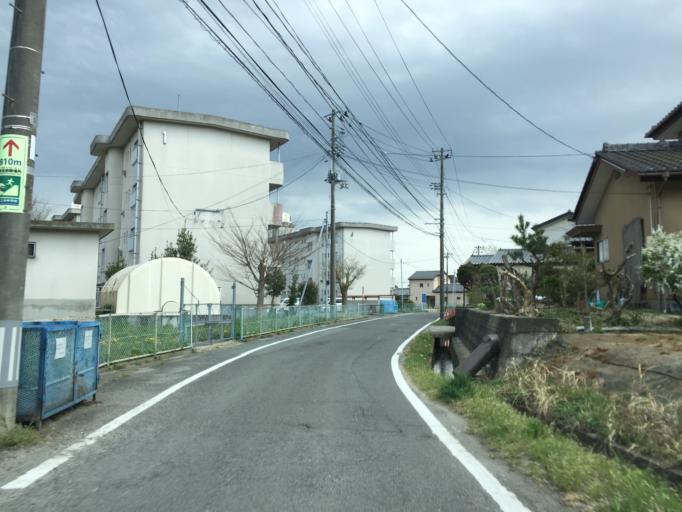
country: JP
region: Fukushima
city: Iwaki
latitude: 37.1484
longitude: 140.9899
